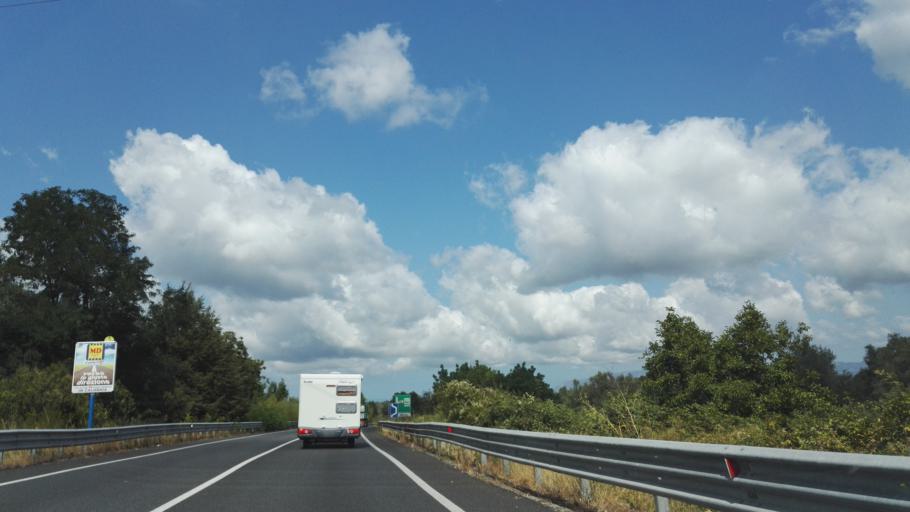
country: IT
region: Calabria
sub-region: Provincia di Reggio Calabria
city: Polistena
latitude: 38.4189
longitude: 16.0683
